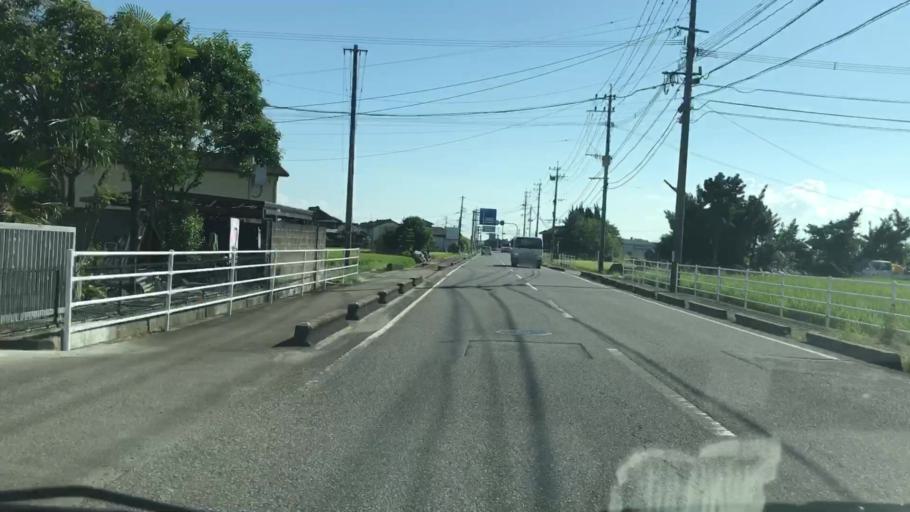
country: JP
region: Saga Prefecture
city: Okawa
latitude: 33.1928
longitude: 130.3330
